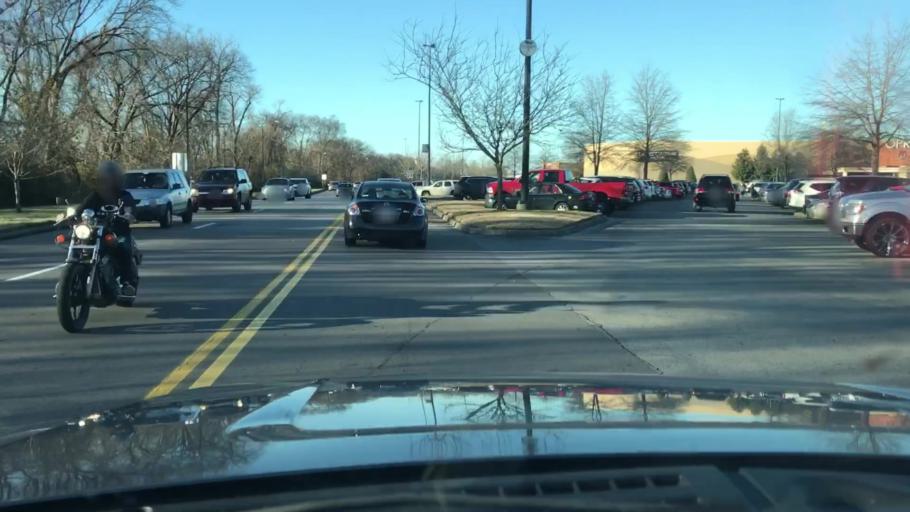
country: US
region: Tennessee
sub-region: Davidson County
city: Lakewood
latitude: 36.1983
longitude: -86.6920
